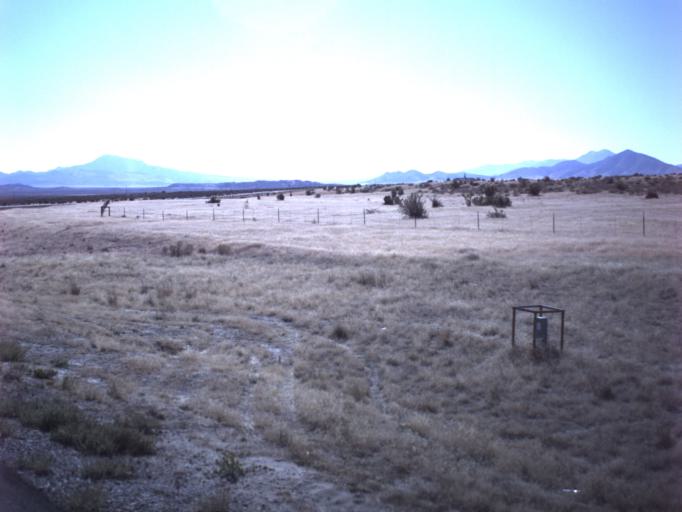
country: US
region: Utah
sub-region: Tooele County
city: Grantsville
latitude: 40.2475
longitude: -112.7252
